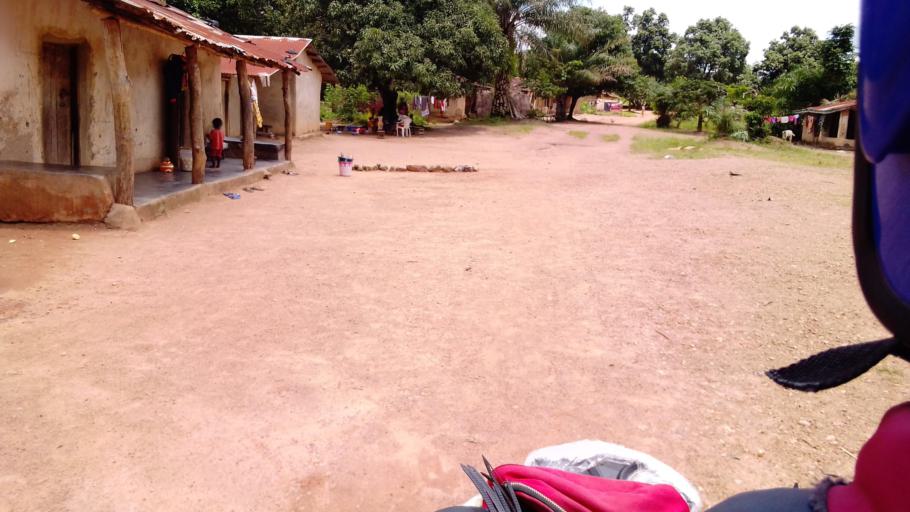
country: SL
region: Eastern Province
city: Koidu
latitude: 8.6778
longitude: -10.9571
